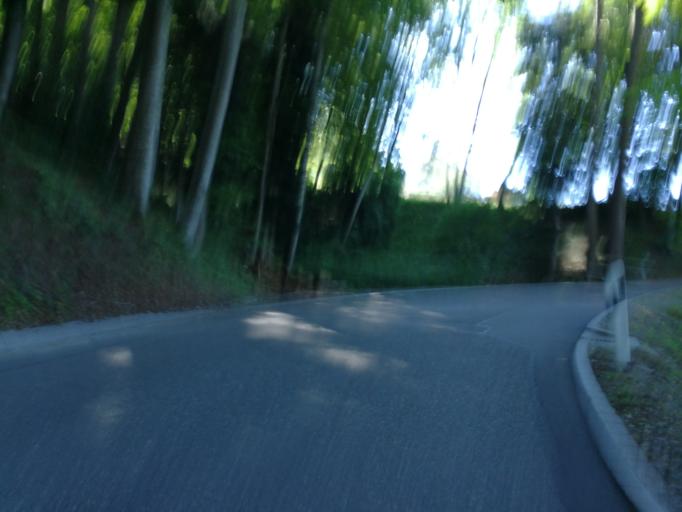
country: CH
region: Zurich
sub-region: Bezirk Hinwil
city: Hadlikon
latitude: 47.2941
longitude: 8.8773
